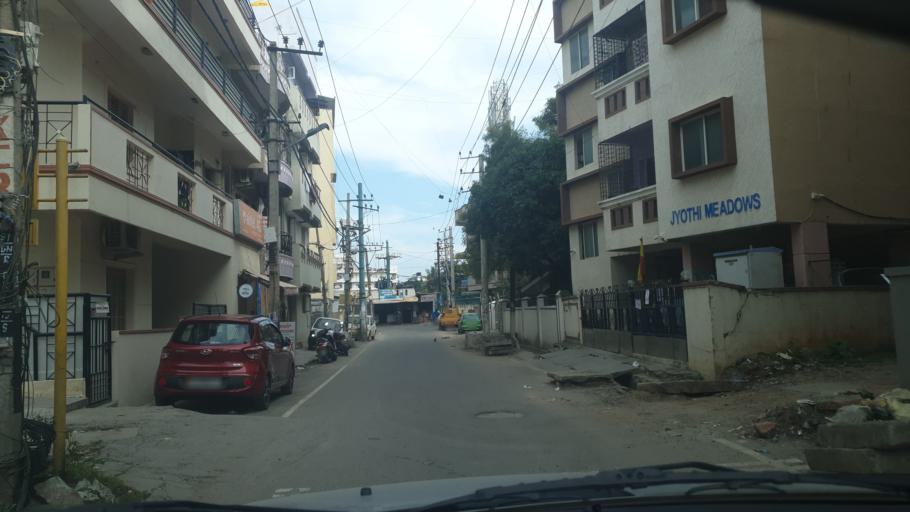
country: IN
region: Karnataka
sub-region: Bangalore Urban
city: Bangalore
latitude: 12.9672
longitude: 77.6721
